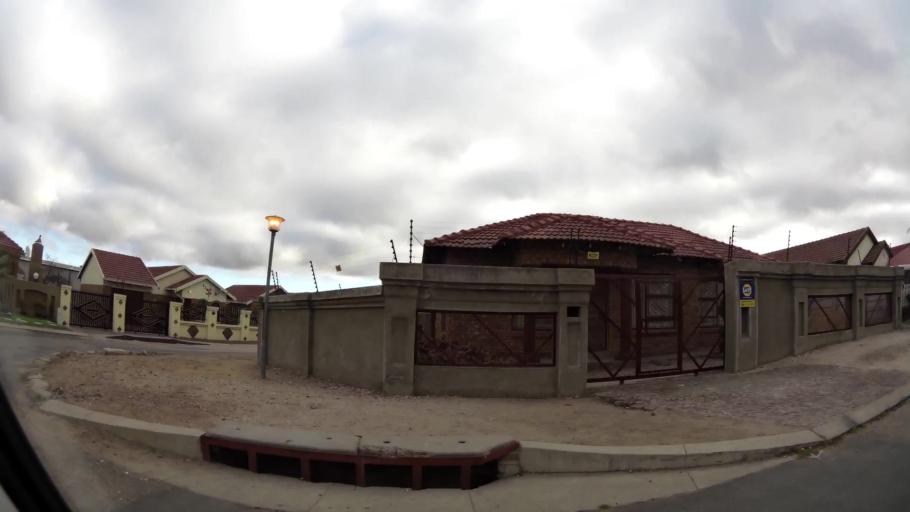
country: ZA
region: Limpopo
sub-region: Capricorn District Municipality
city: Polokwane
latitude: -23.9209
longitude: 29.4483
